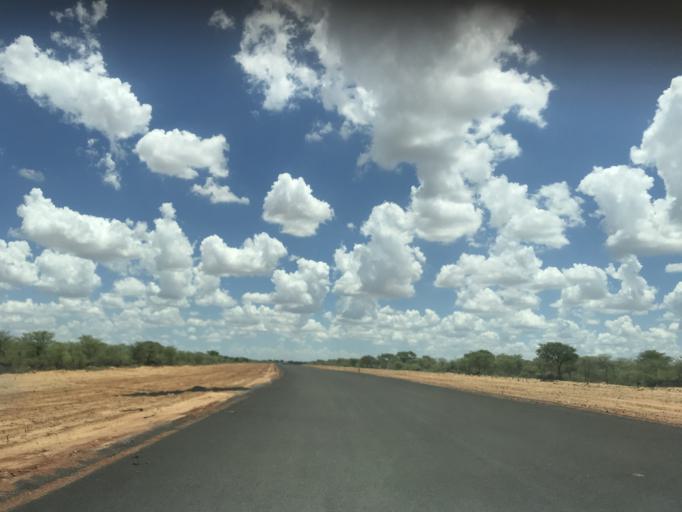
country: BW
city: Mabuli
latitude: -25.8047
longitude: 24.6950
